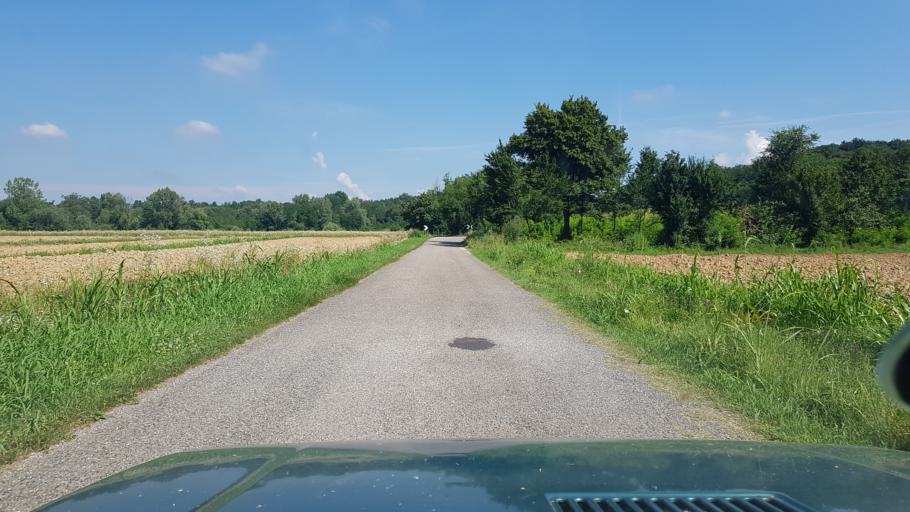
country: IT
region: Friuli Venezia Giulia
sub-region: Provincia di Gorizia
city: San Lorenzo Isontino
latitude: 45.9378
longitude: 13.5300
